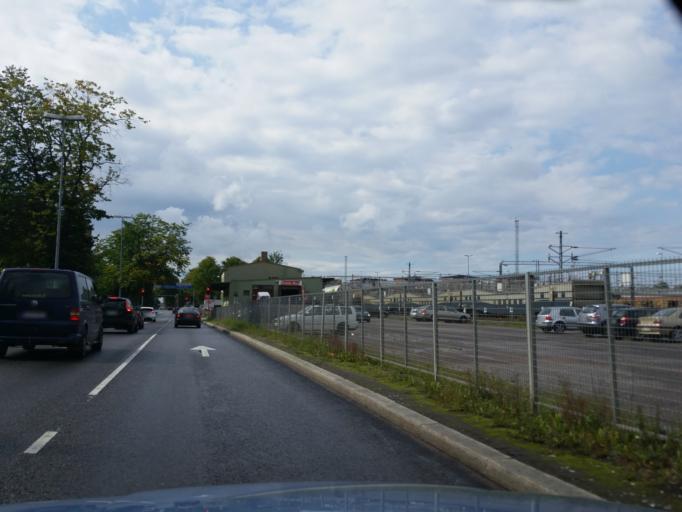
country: FI
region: Varsinais-Suomi
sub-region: Turku
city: Turku
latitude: 60.4550
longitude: 22.2578
